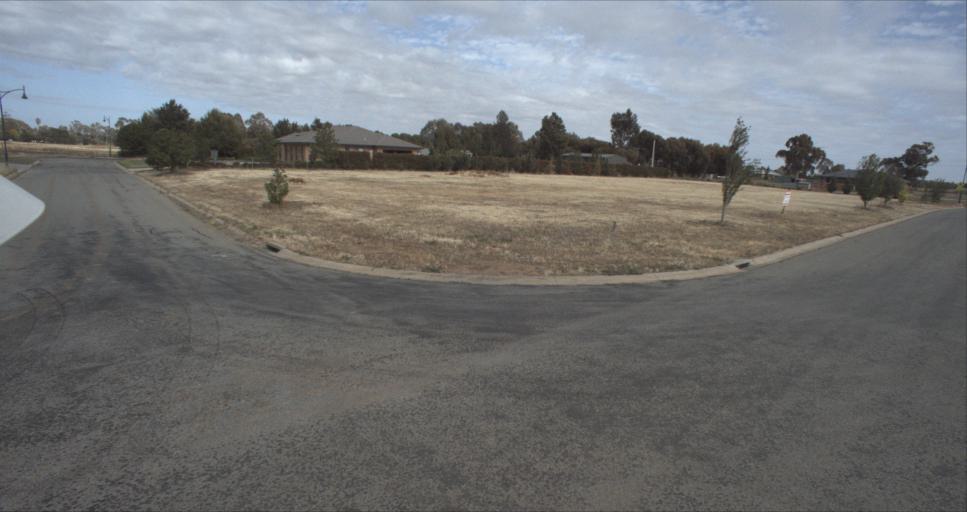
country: AU
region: New South Wales
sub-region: Leeton
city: Leeton
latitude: -34.5592
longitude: 146.4277
